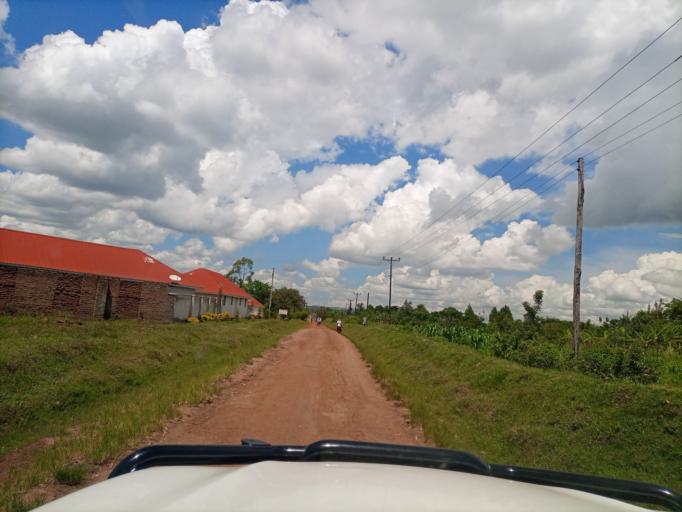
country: UG
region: Eastern Region
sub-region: Tororo District
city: Tororo
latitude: 0.6455
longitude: 33.9956
